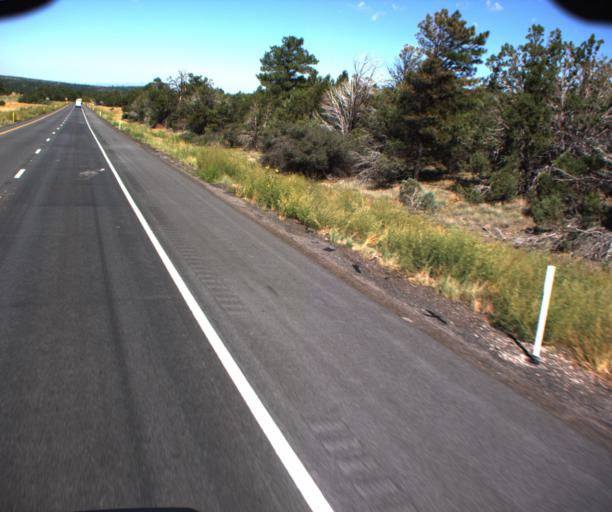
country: US
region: Arizona
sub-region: Coconino County
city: Williams
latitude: 35.2226
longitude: -112.2605
